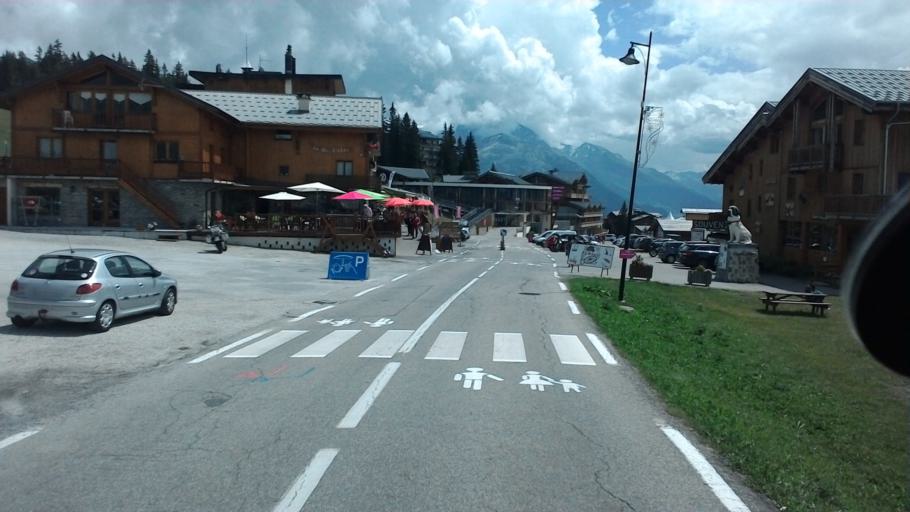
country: FR
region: Rhone-Alpes
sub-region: Departement de la Savoie
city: Seez
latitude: 45.6299
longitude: 6.8469
